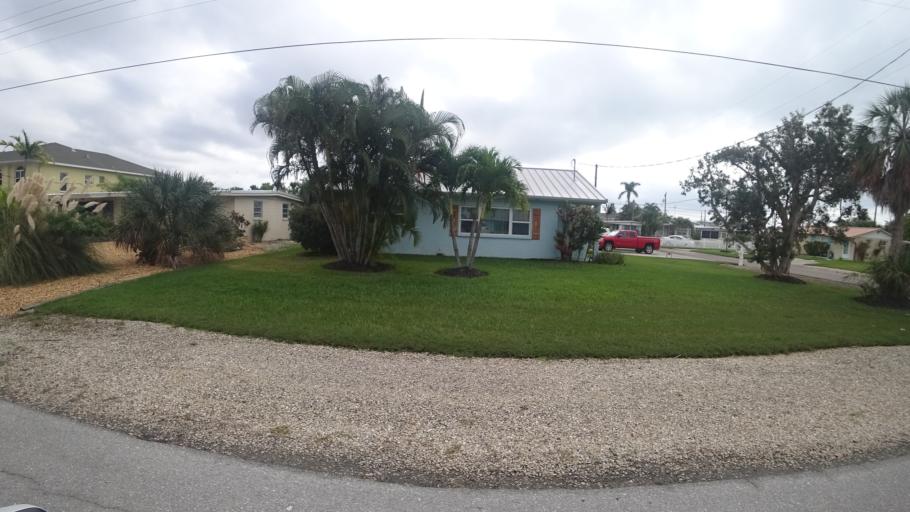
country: US
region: Florida
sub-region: Manatee County
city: Holmes Beach
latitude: 27.4857
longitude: -82.7039
